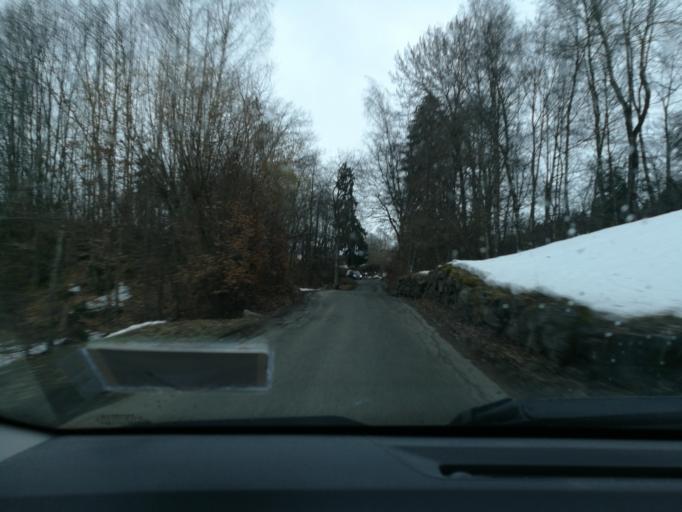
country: FR
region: Rhone-Alpes
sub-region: Departement de la Haute-Savoie
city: Domancy
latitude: 45.9161
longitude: 6.6301
